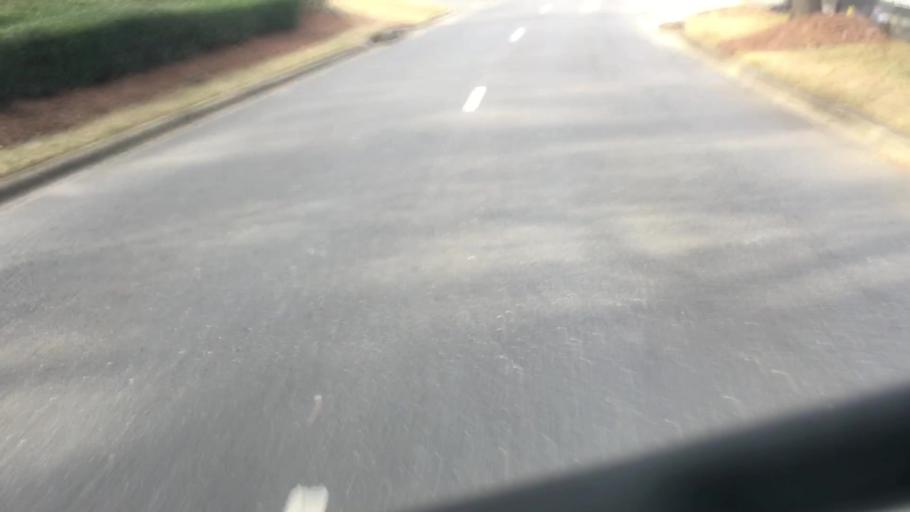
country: US
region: Alabama
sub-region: Jefferson County
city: Cahaba Heights
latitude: 33.4844
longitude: -86.7080
